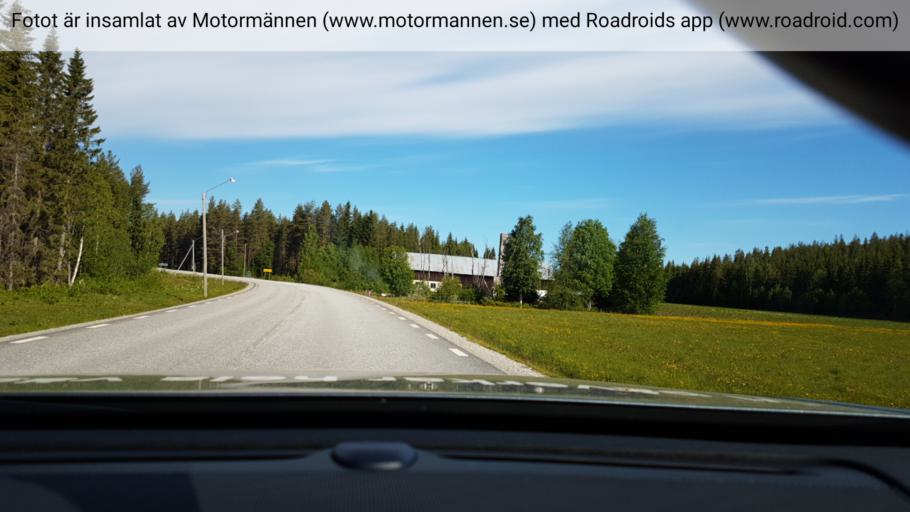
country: SE
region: Vaesterbotten
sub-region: Vindelns Kommun
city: Vindeln
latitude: 64.2005
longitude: 19.4491
